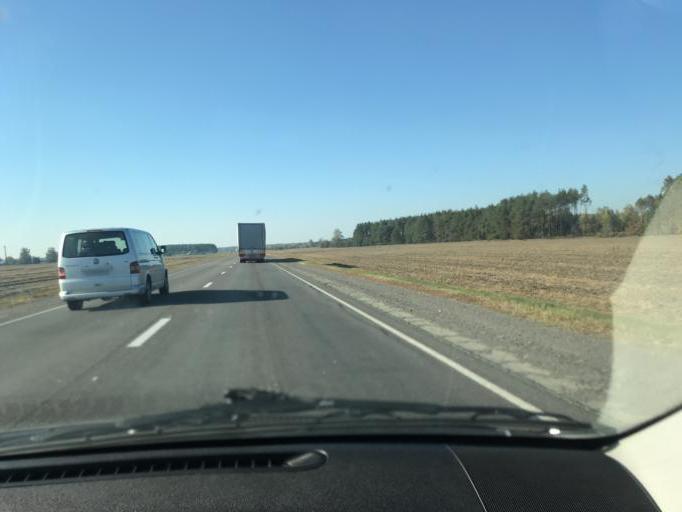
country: BY
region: Brest
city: Davyd-Haradok
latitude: 52.2402
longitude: 27.2051
